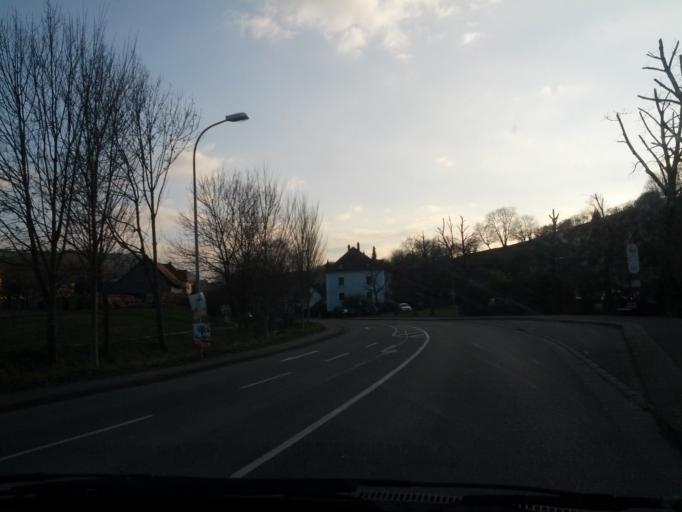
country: DE
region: Baden-Wuerttemberg
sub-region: Freiburg Region
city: Merzhausen
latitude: 47.9584
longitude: 7.8308
